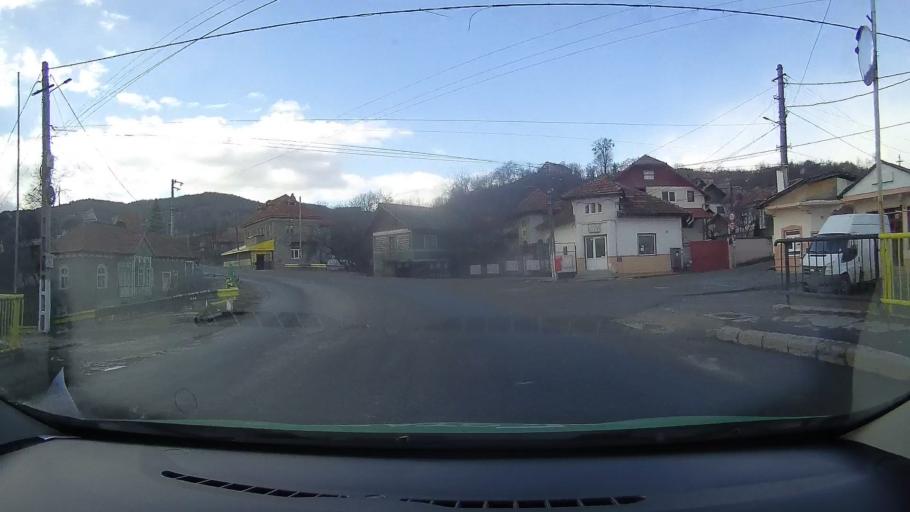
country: RO
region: Dambovita
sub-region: Comuna Pietrosita
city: Pietrosita
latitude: 45.1863
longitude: 25.4383
